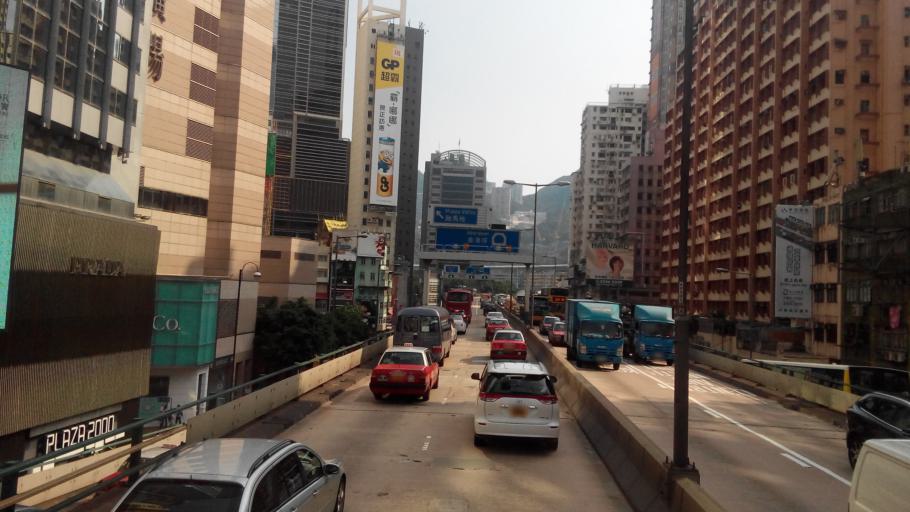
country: HK
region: Wanchai
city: Wan Chai
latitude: 22.2791
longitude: 114.1813
